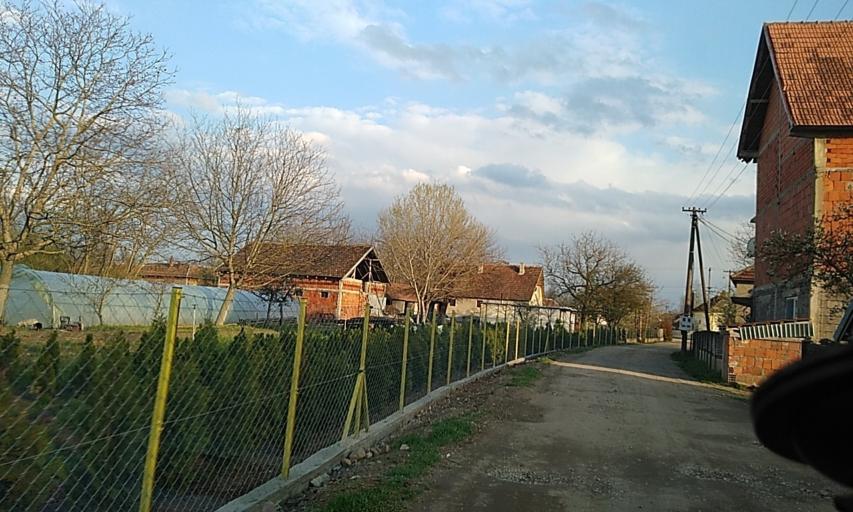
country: RS
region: Central Serbia
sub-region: Nisavski Okrug
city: Razanj
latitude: 43.5928
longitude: 21.6099
